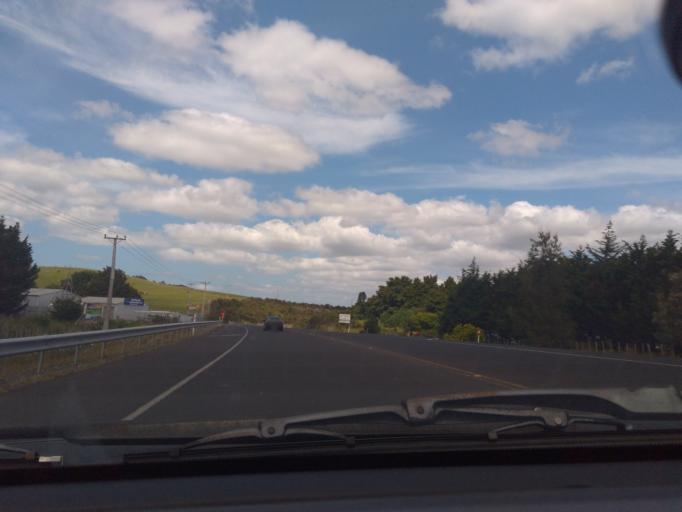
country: NZ
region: Northland
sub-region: Far North District
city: Kerikeri
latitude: -35.2715
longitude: 173.9445
